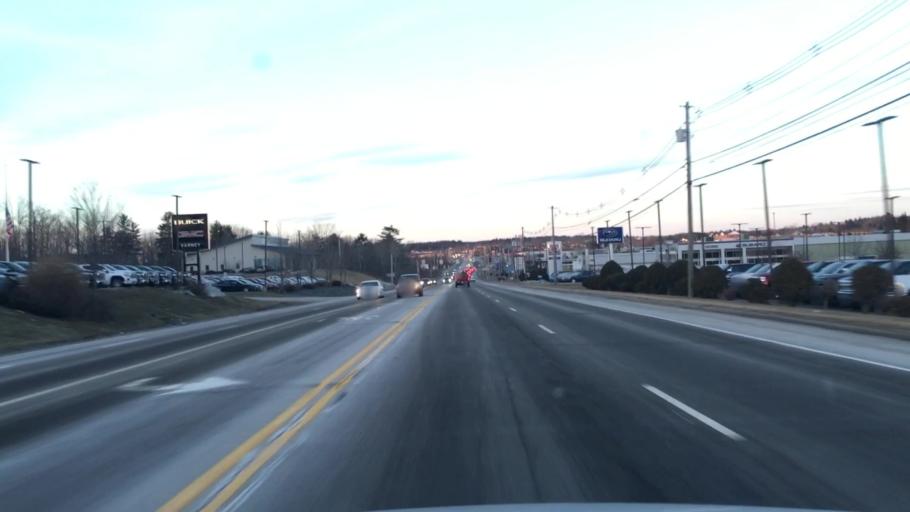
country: US
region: Maine
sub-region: Penobscot County
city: Brewer
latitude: 44.8230
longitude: -68.7397
